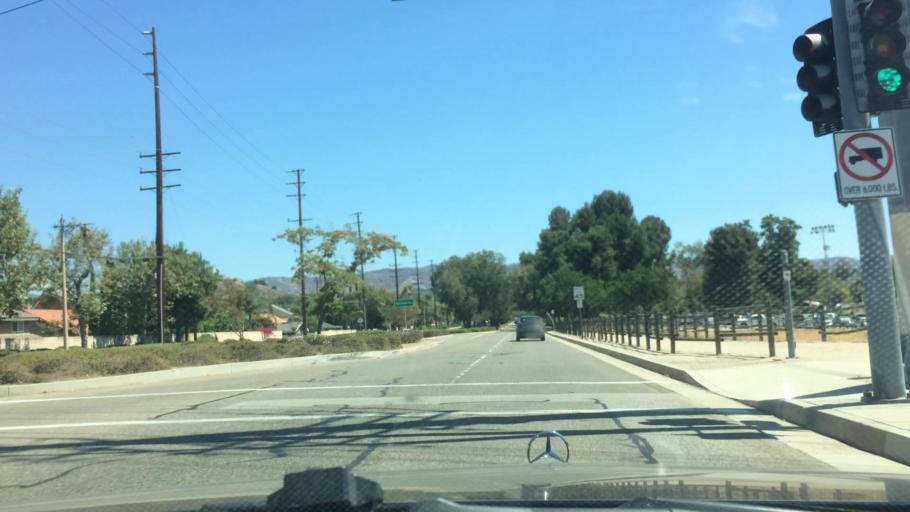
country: US
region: California
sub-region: Orange County
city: Yorba Linda
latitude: 33.8641
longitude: -117.7753
